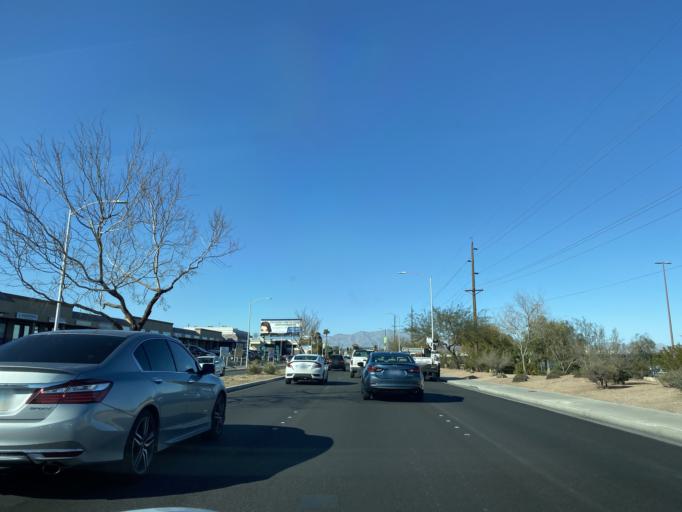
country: US
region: Nevada
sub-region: Clark County
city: Las Vegas
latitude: 36.1603
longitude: -115.1925
